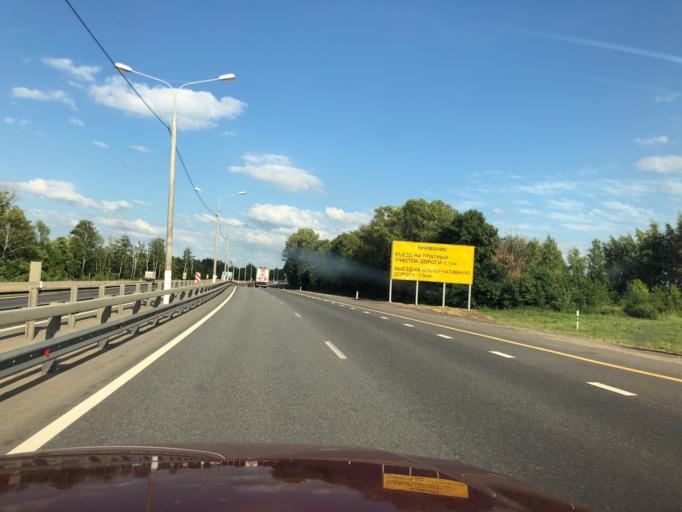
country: RU
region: Lipetsk
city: Zadonsk
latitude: 52.4415
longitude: 38.7967
